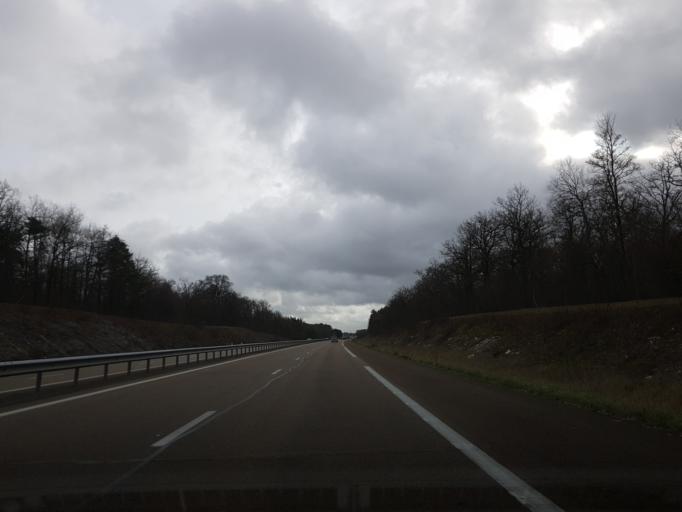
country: FR
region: Champagne-Ardenne
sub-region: Departement de la Haute-Marne
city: Chamarandes-Choignes
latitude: 47.9935
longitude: 5.1238
